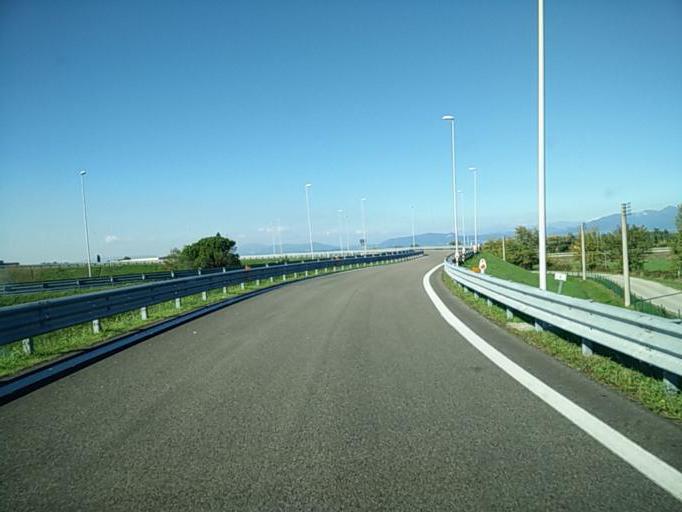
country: IT
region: Lombardy
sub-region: Provincia di Brescia
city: San Martino della Battaglia
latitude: 45.4342
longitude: 10.6127
